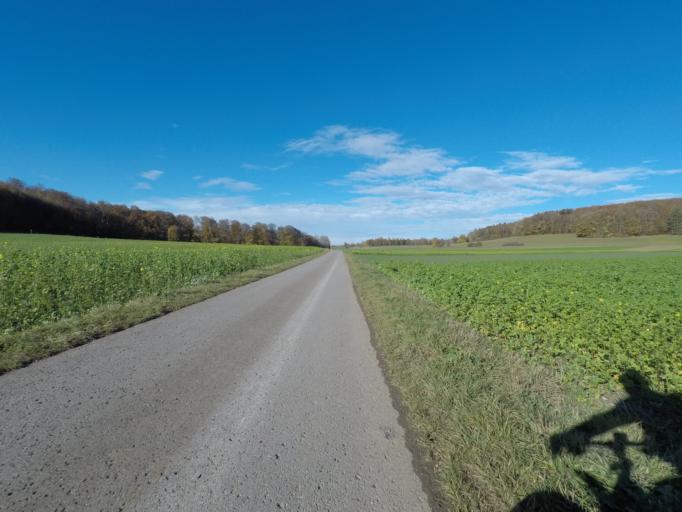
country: DE
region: Baden-Wuerttemberg
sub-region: Tuebingen Region
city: Pfullingen
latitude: 48.4160
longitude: 9.2112
